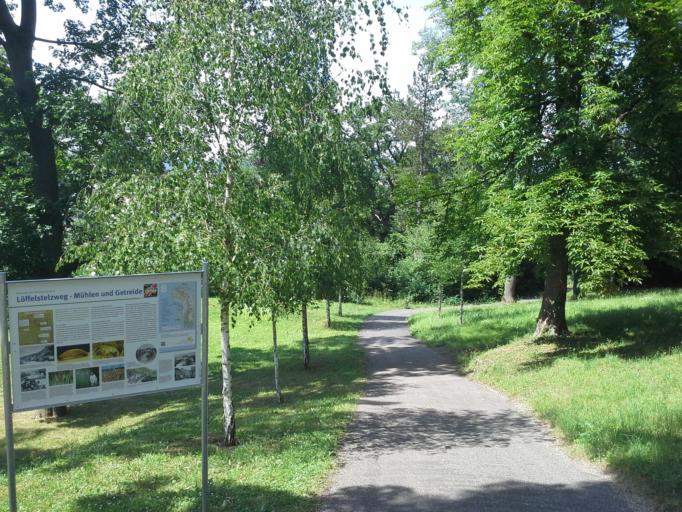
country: DE
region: Baden-Wuerttemberg
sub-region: Karlsruhe Region
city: Muhlacker
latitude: 48.9417
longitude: 8.8460
